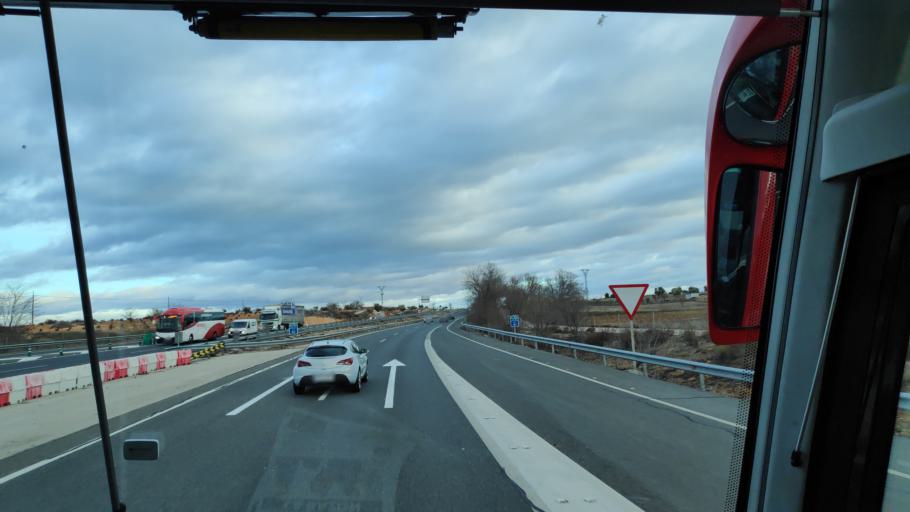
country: ES
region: Madrid
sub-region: Provincia de Madrid
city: Villarejo de Salvanes
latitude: 40.1619
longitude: -3.2650
